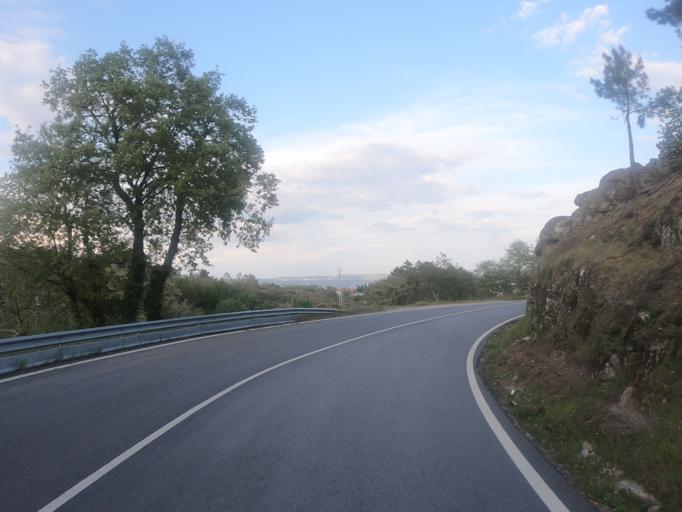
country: PT
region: Vila Real
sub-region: Santa Marta de Penaguiao
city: Santa Marta de Penaguiao
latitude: 41.2829
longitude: -7.8204
